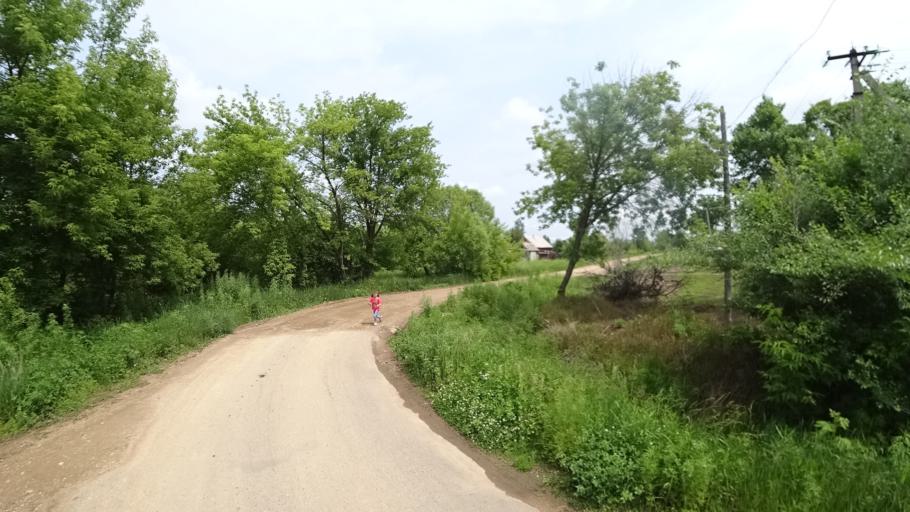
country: RU
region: Primorskiy
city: Novosysoyevka
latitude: 44.2388
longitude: 133.3580
